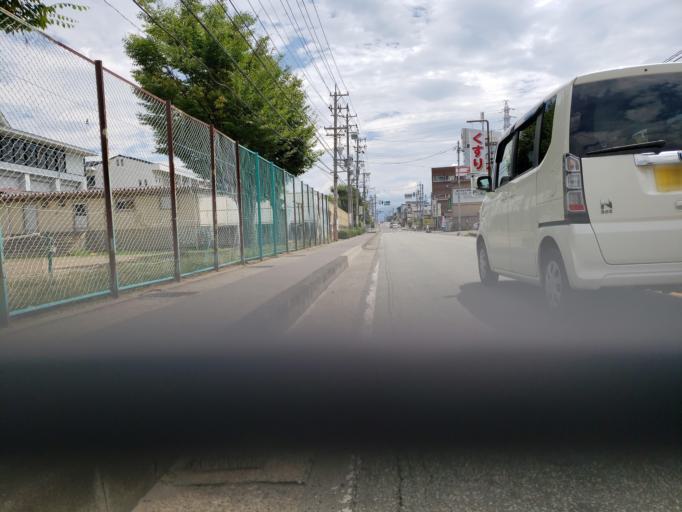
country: JP
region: Nagano
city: Nagano-shi
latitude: 36.6330
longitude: 138.1752
